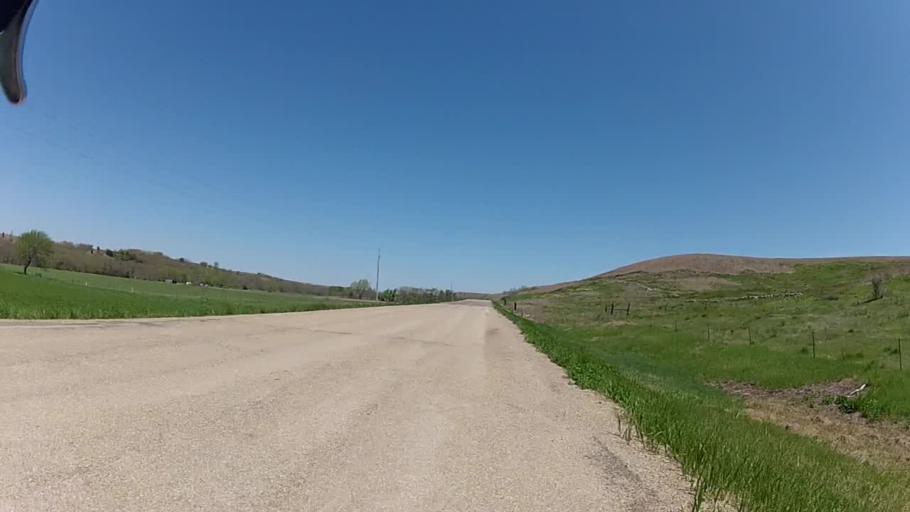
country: US
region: Kansas
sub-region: Riley County
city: Ogden
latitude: 38.9750
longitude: -96.5876
